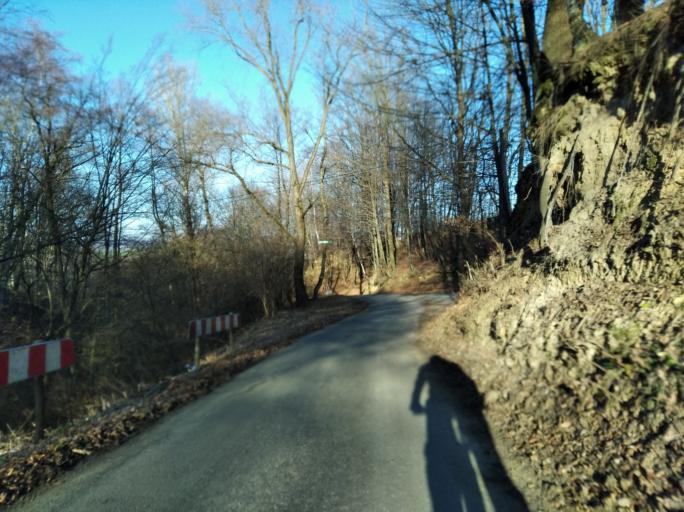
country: PL
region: Subcarpathian Voivodeship
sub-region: Powiat strzyzowski
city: Wysoka Strzyzowska
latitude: 49.8556
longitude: 21.7434
